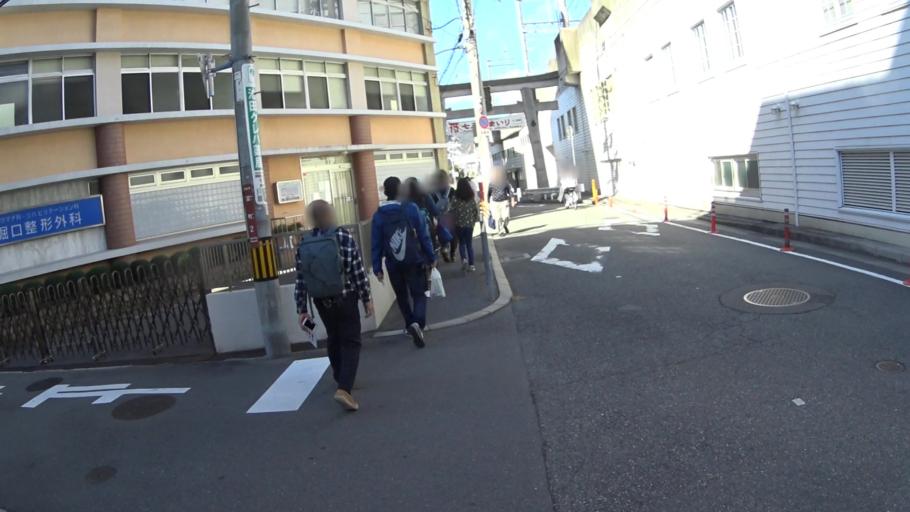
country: JP
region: Osaka
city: Ikeda
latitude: 34.8222
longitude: 135.4245
